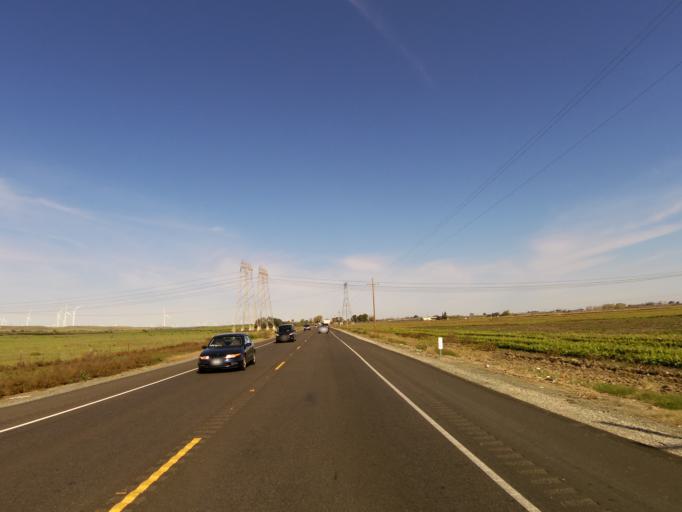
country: US
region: California
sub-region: Contra Costa County
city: Oakley
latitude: 38.0705
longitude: -121.7350
